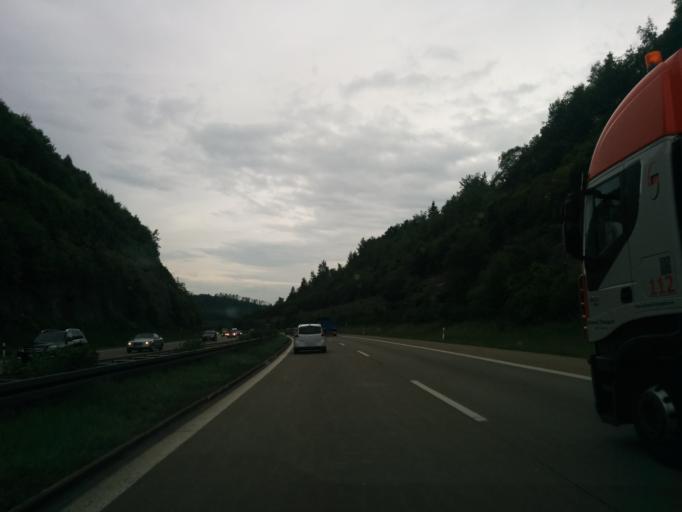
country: DE
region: Baden-Wuerttemberg
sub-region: Regierungsbezirk Stuttgart
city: Westhausen
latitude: 48.8611
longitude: 10.1947
